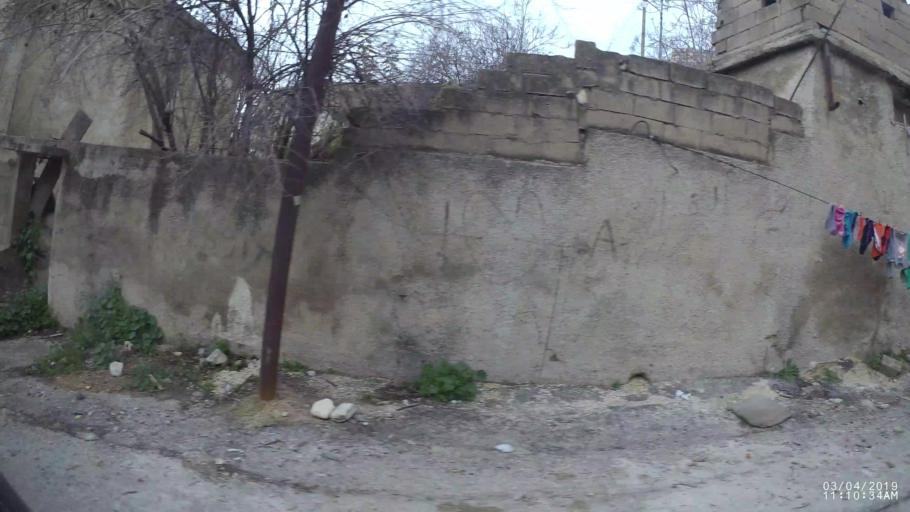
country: JO
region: Amman
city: Wadi as Sir
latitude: 31.9527
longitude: 35.8174
